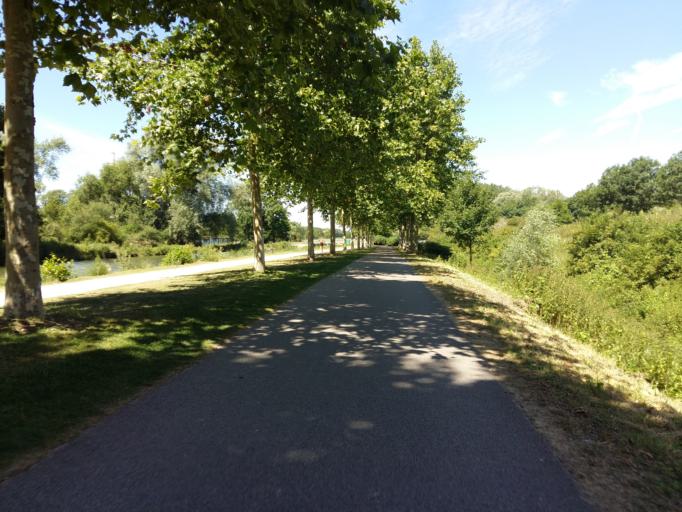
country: FR
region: Picardie
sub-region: Departement de la Somme
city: Dreuil-les-Amiens
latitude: 49.9178
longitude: 2.2604
